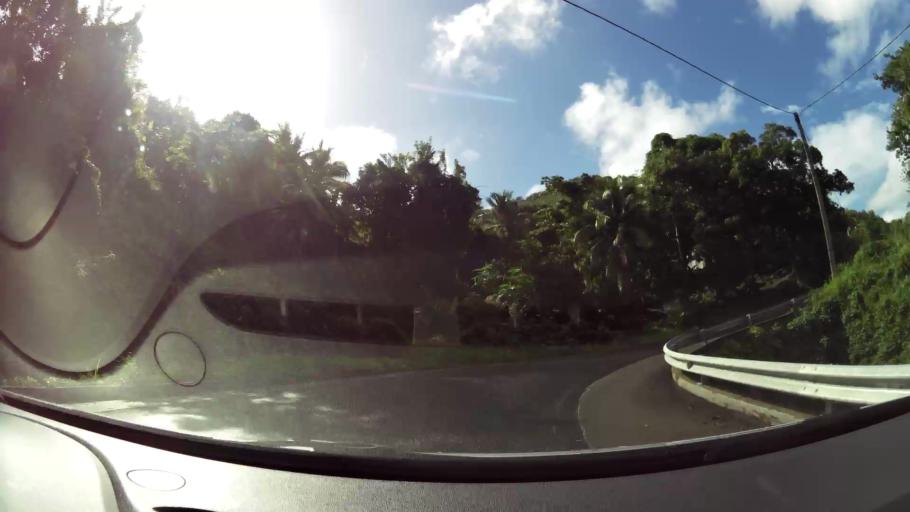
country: MQ
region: Martinique
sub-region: Martinique
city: Les Trois-Ilets
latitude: 14.5291
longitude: -61.0720
